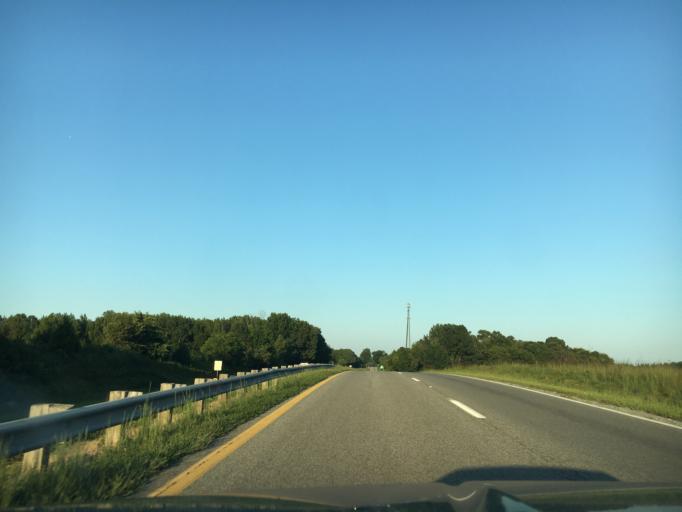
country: US
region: Virginia
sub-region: Halifax County
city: Mountain Road
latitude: 36.5839
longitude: -79.1452
